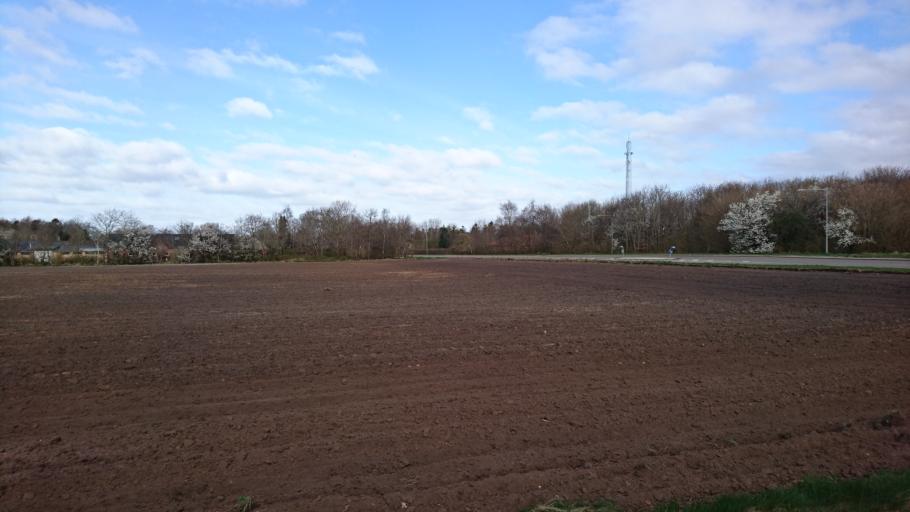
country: DK
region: Central Jutland
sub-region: Herning Kommune
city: Sunds
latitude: 56.1985
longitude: 9.0275
